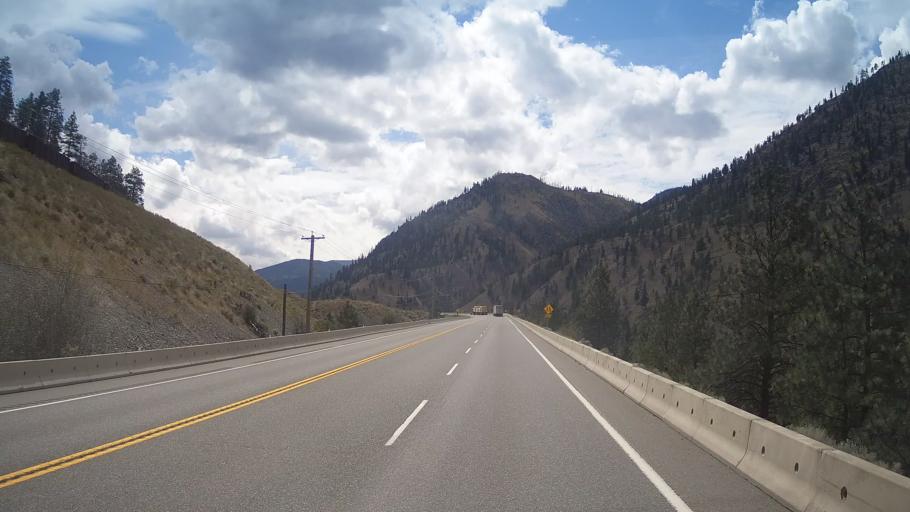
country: CA
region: British Columbia
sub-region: Thompson-Nicola Regional District
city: Ashcroft
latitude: 50.3162
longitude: -121.3944
